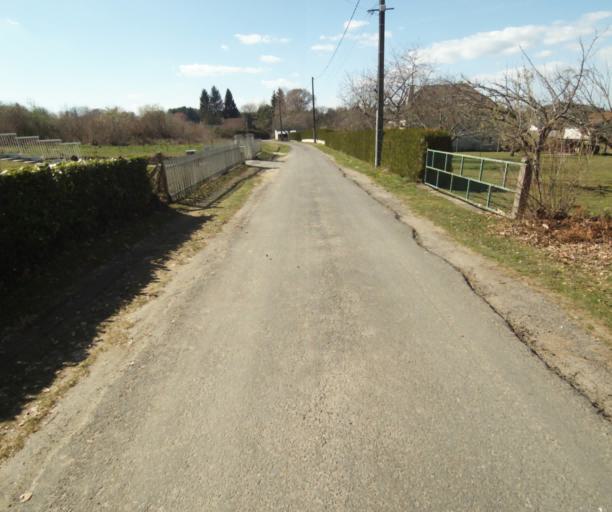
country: FR
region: Limousin
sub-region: Departement de la Correze
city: Saint-Mexant
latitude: 45.2867
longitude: 1.6673
